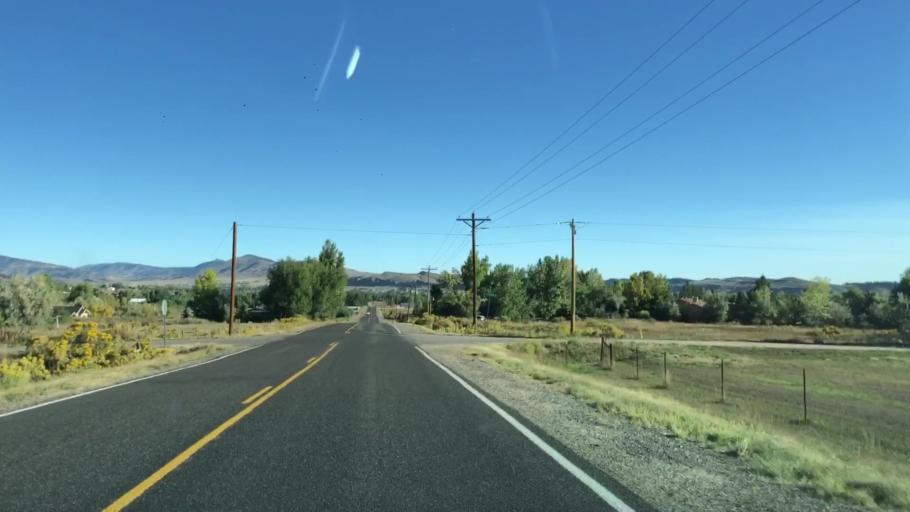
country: US
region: Colorado
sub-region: Larimer County
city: Loveland
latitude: 40.3833
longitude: -105.1634
